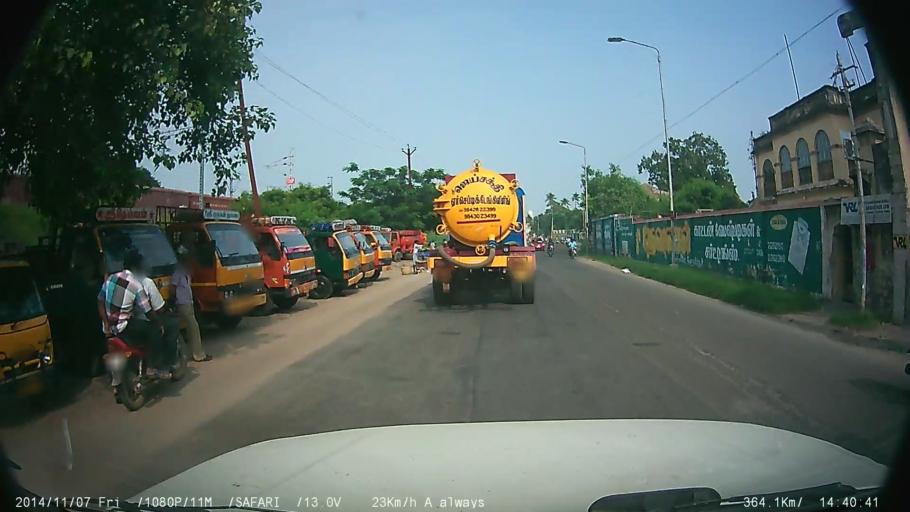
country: IN
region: Tamil Nadu
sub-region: Tiruppur
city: Tiruppur
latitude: 11.1115
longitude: 77.3515
